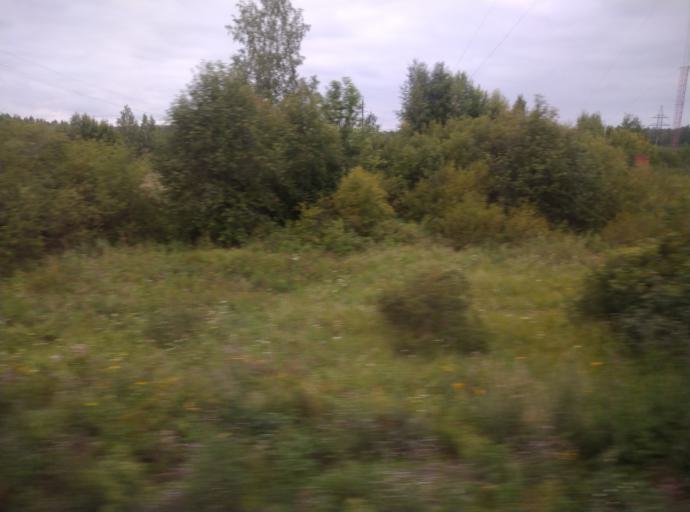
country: RU
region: Kostroma
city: Kosmynino
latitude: 57.5823
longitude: 40.7519
